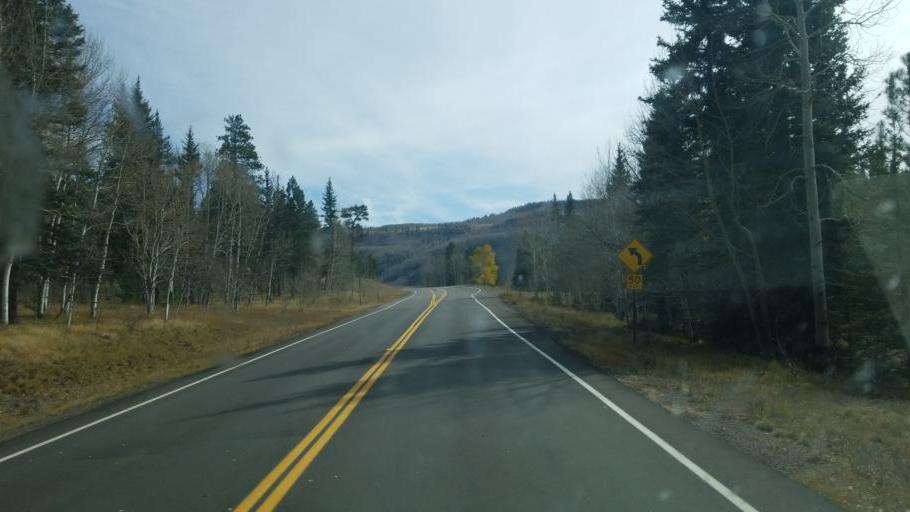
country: US
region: Colorado
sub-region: Conejos County
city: Conejos
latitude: 37.0846
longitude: -106.3007
